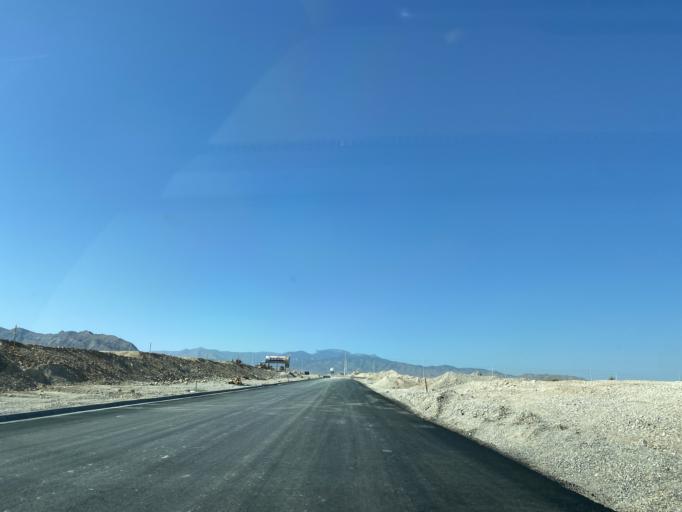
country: US
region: Nevada
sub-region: Clark County
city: Summerlin South
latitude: 36.3214
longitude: -115.3180
